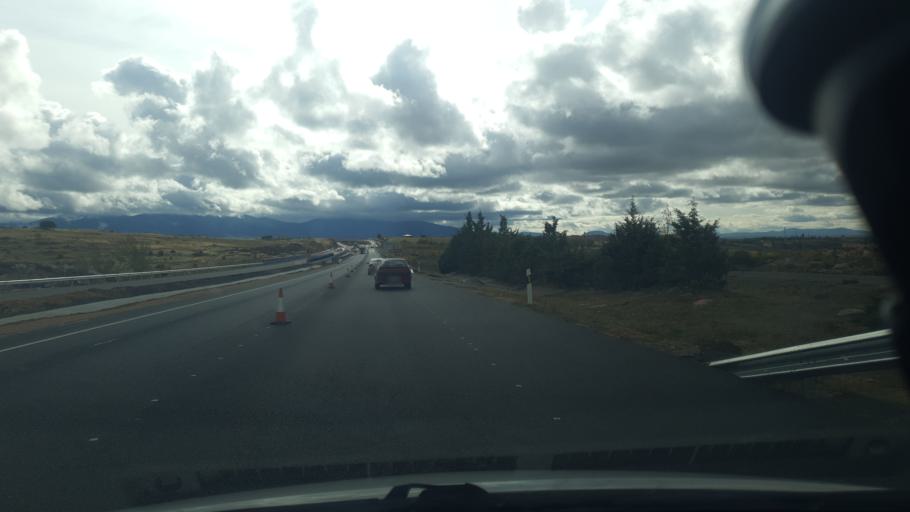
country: ES
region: Castille and Leon
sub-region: Provincia de Segovia
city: San Cristobal de Segovia
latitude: 40.9633
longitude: -4.0873
